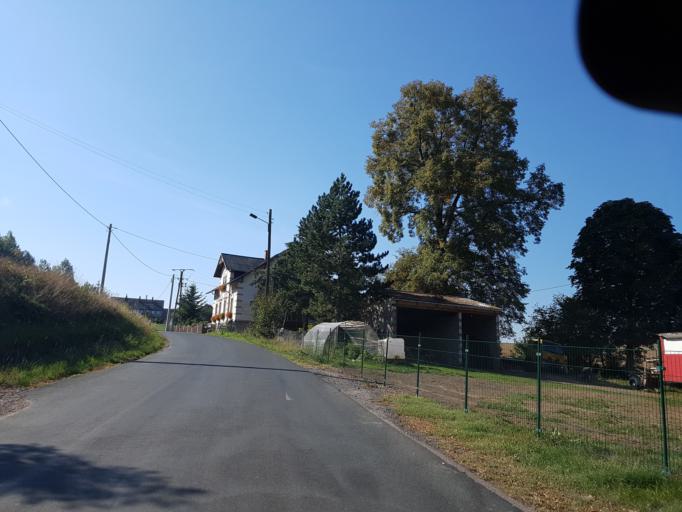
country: DE
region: Saxony
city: Kriebstein
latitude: 51.0625
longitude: 13.0095
